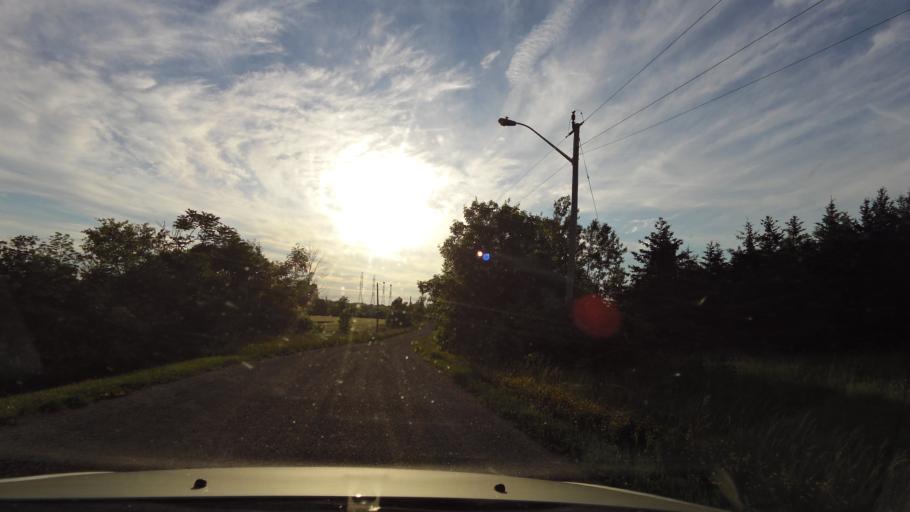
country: CA
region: Ontario
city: Ancaster
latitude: 43.0696
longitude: -79.9654
